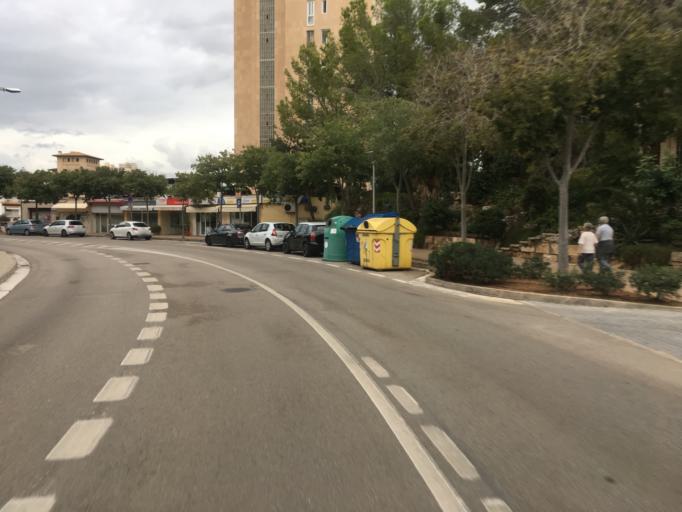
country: ES
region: Balearic Islands
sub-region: Illes Balears
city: Palma
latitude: 39.5452
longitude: 2.5957
